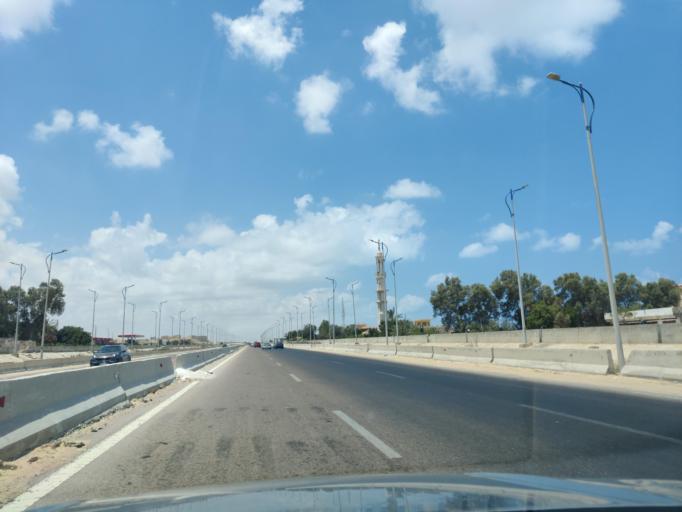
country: EG
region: Alexandria
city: Alexandria
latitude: 30.9532
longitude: 29.5286
